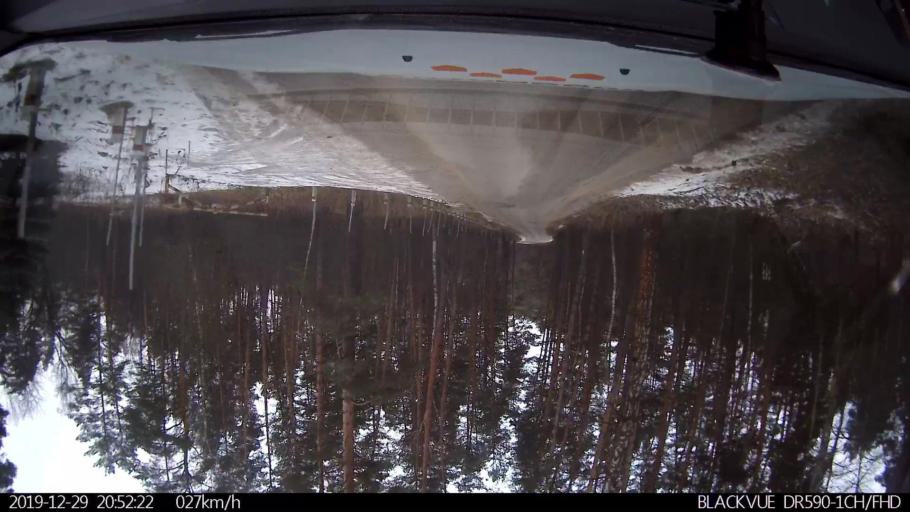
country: RU
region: Nizjnij Novgorod
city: Afonino
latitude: 56.1767
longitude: 43.9933
